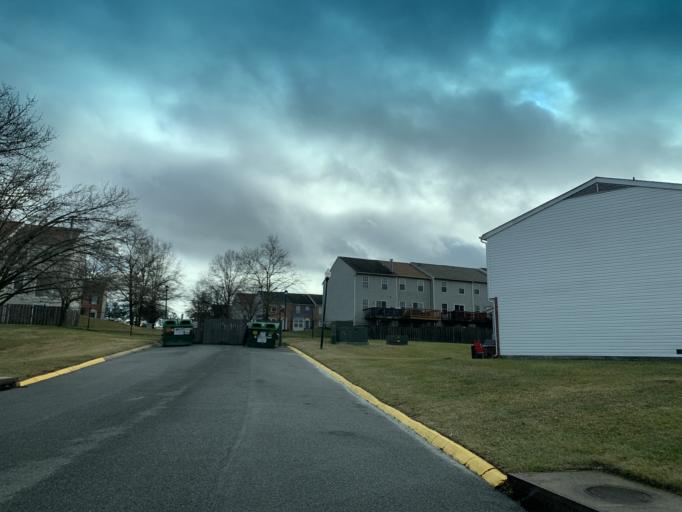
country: US
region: Maryland
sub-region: Harford County
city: Edgewood
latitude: 39.4253
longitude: -76.3196
